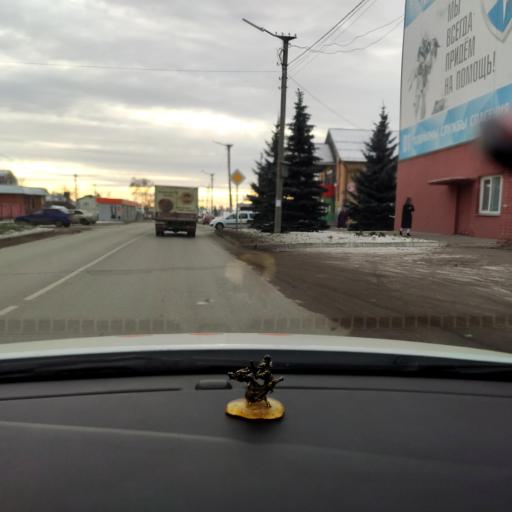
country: RU
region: Tatarstan
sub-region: Zelenodol'skiy Rayon
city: Zelenodolsk
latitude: 55.8559
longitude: 48.5309
